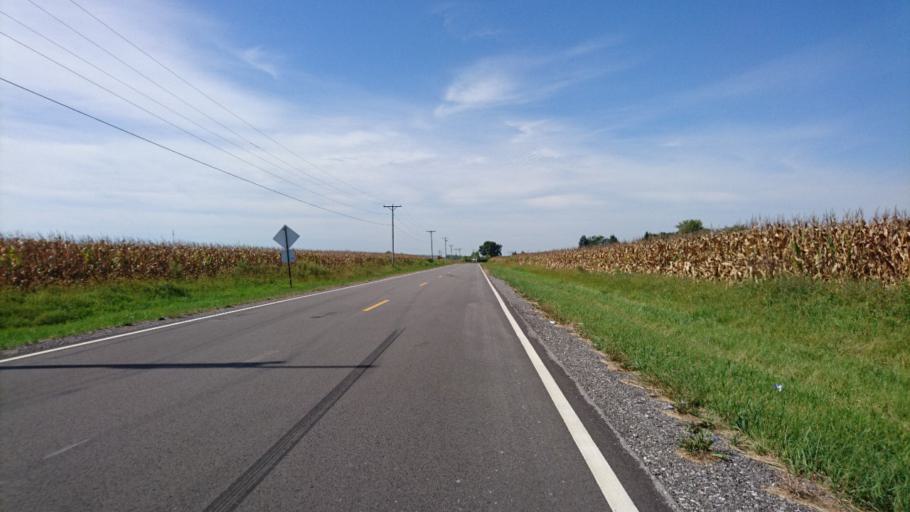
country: US
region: Illinois
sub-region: Will County
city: Elwood
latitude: 41.4069
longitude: -88.0939
